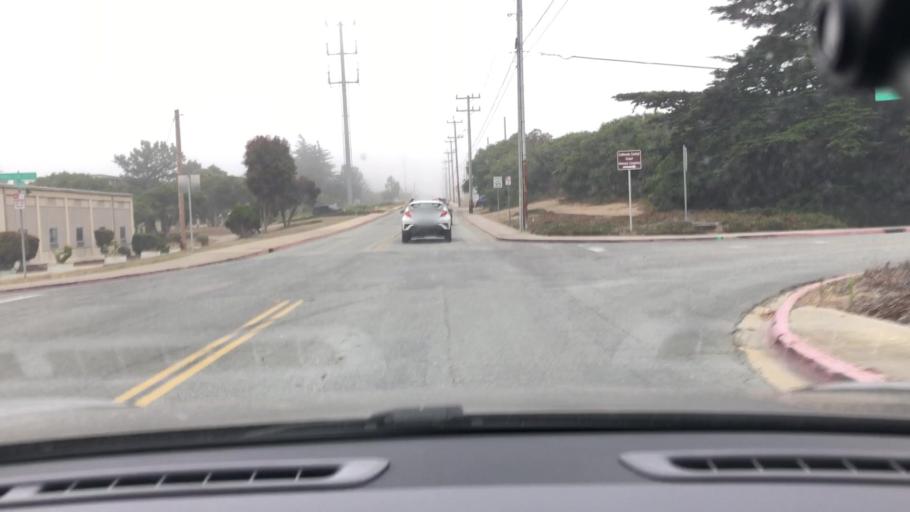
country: US
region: California
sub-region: Monterey County
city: Marina
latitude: 36.6439
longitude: -121.7982
